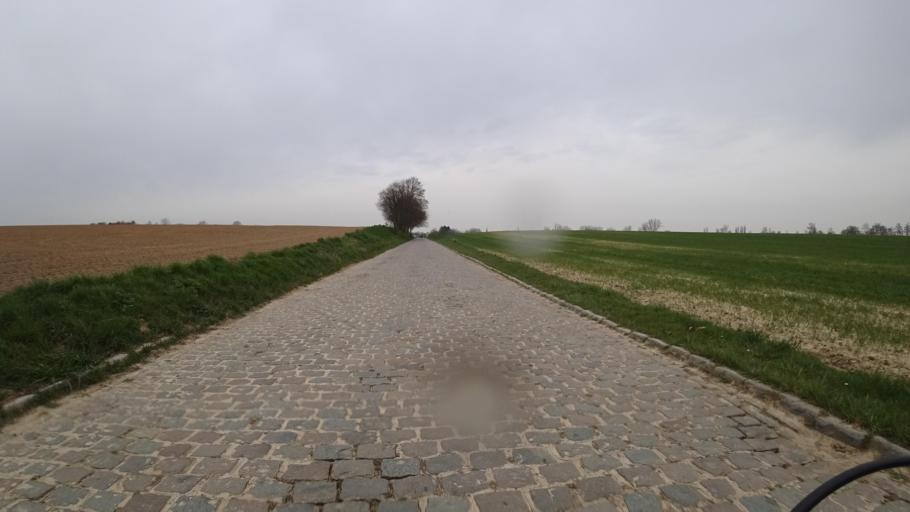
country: BE
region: Wallonia
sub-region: Province du Brabant Wallon
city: Walhain-Saint-Paul
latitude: 50.6073
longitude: 4.6993
